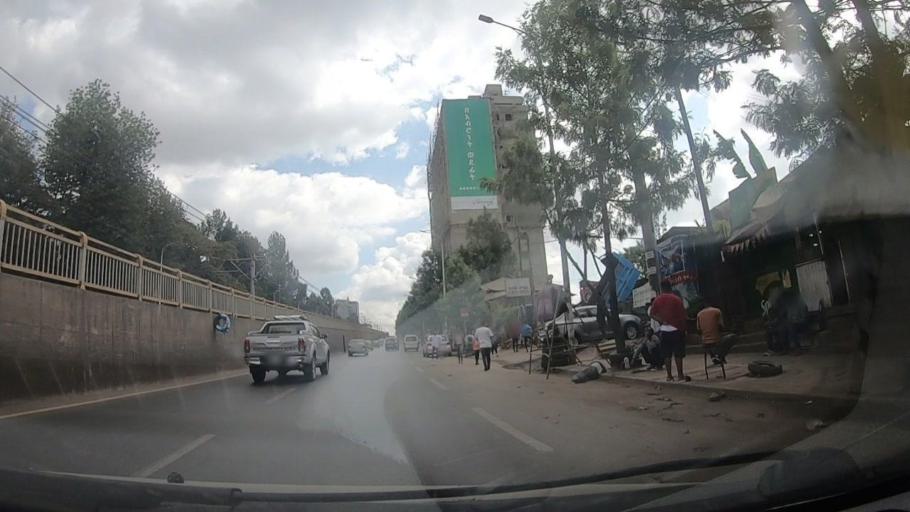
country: ET
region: Adis Abeba
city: Addis Ababa
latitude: 9.0119
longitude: 38.7299
